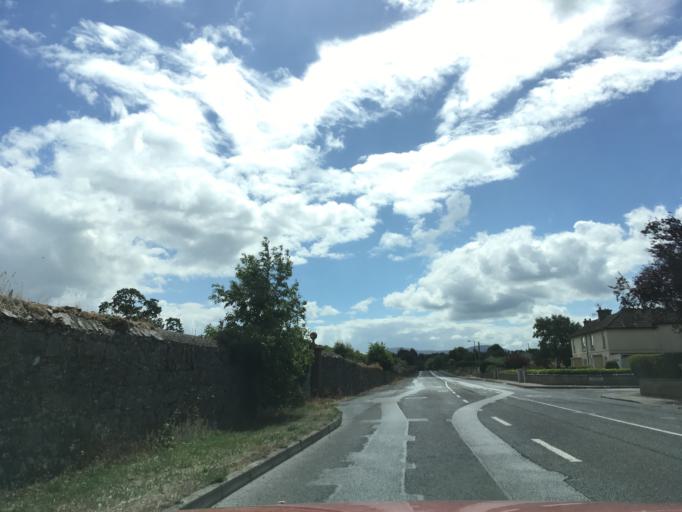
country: IE
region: Munster
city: Cahir
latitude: 52.3703
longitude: -7.9315
